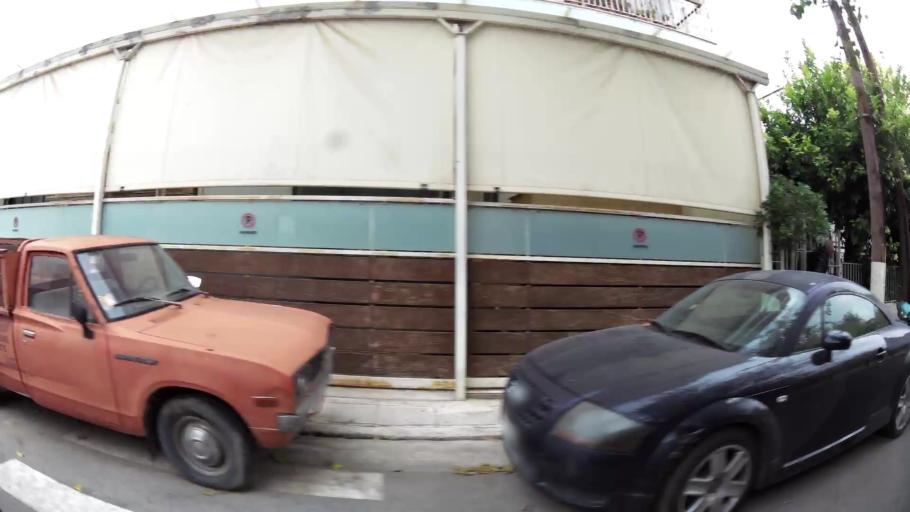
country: GR
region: Attica
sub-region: Nomarchia Athinas
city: Aigaleo
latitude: 37.9833
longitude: 23.6807
